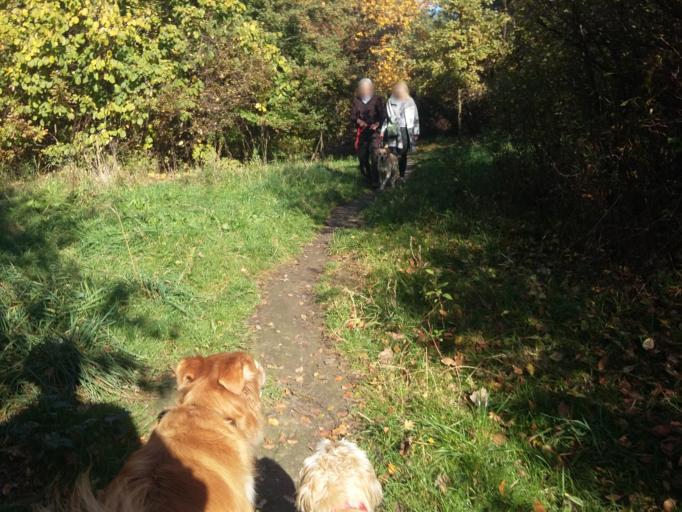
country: PL
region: Lodz Voivodeship
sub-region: Powiat pabianicki
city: Ksawerow
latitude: 51.7361
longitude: 19.4050
